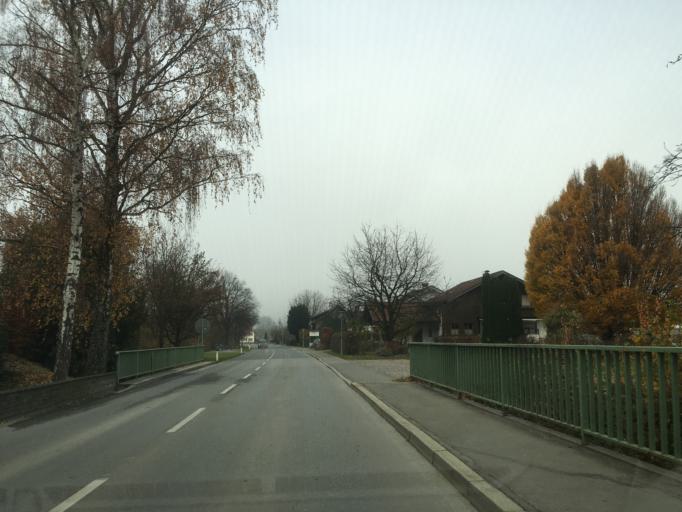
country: AT
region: Vorarlberg
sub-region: Politischer Bezirk Feldkirch
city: Koblach
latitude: 47.3242
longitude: 9.6007
